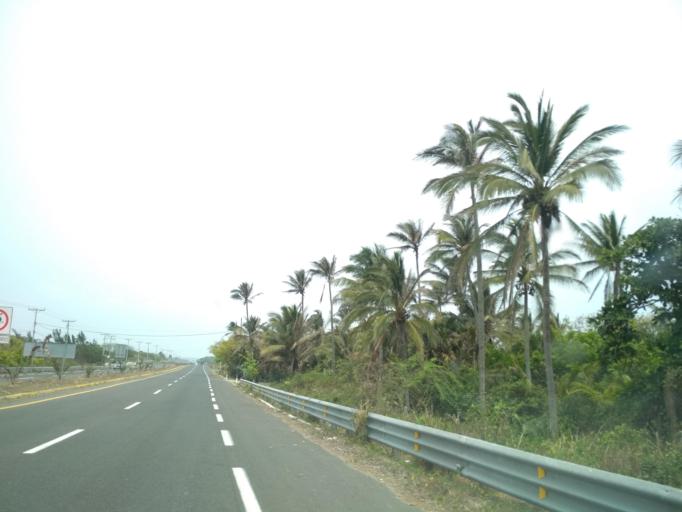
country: MX
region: Veracruz
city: Anton Lizardo
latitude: 19.0522
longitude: -96.0181
